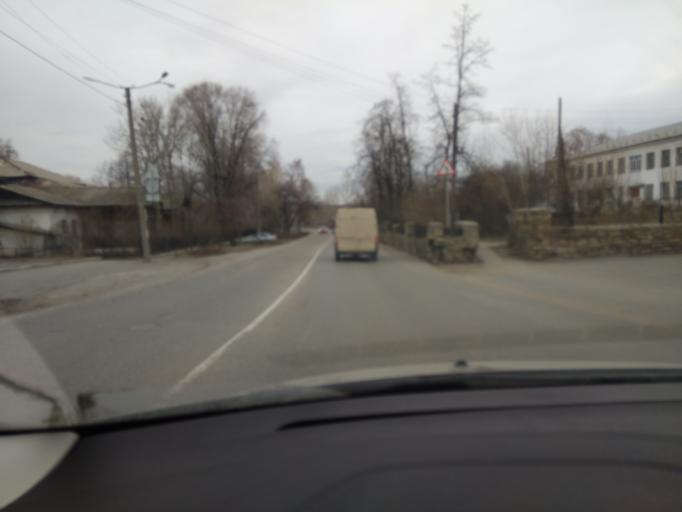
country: RU
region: Chelyabinsk
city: Kyshtym
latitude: 55.7038
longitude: 60.5319
